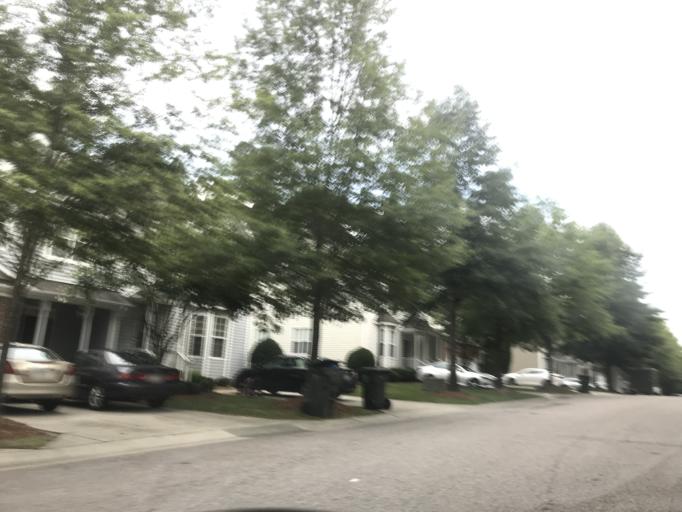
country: US
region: North Carolina
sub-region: Wake County
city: Knightdale
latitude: 35.8636
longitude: -78.5636
